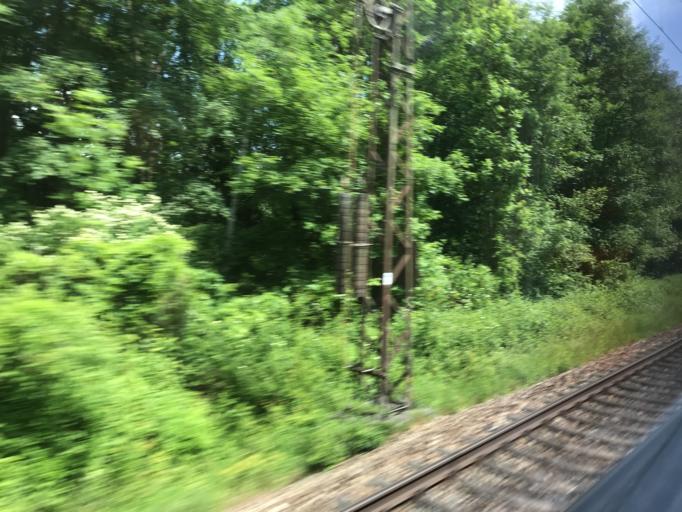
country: DE
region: Bavaria
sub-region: Swabia
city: Guenzburg
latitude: 48.4645
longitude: 10.2931
